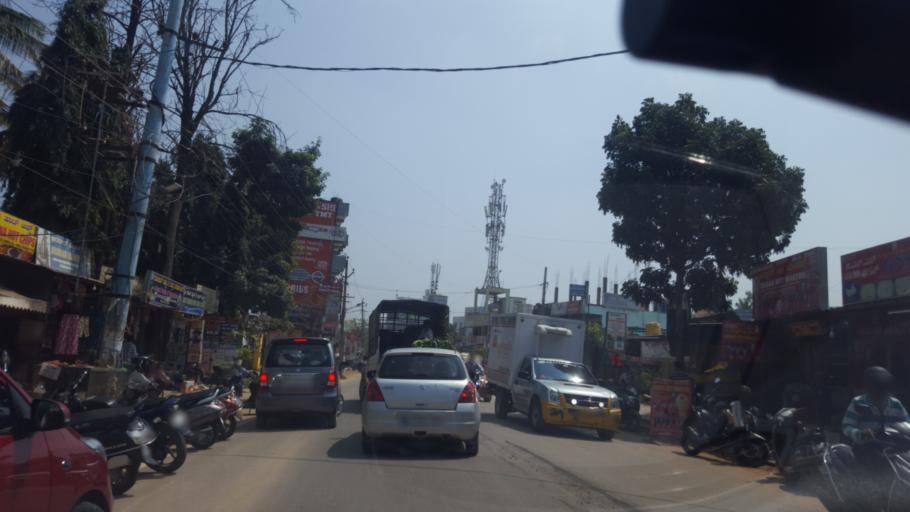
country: IN
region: Karnataka
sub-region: Bangalore Urban
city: Bangalore
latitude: 12.9372
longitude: 77.7024
